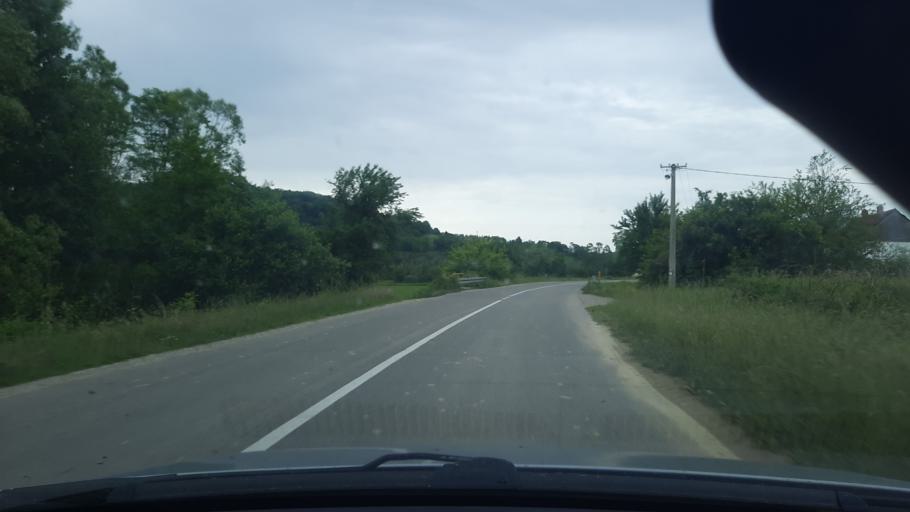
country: RS
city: Jarebice
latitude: 44.4954
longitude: 19.4866
